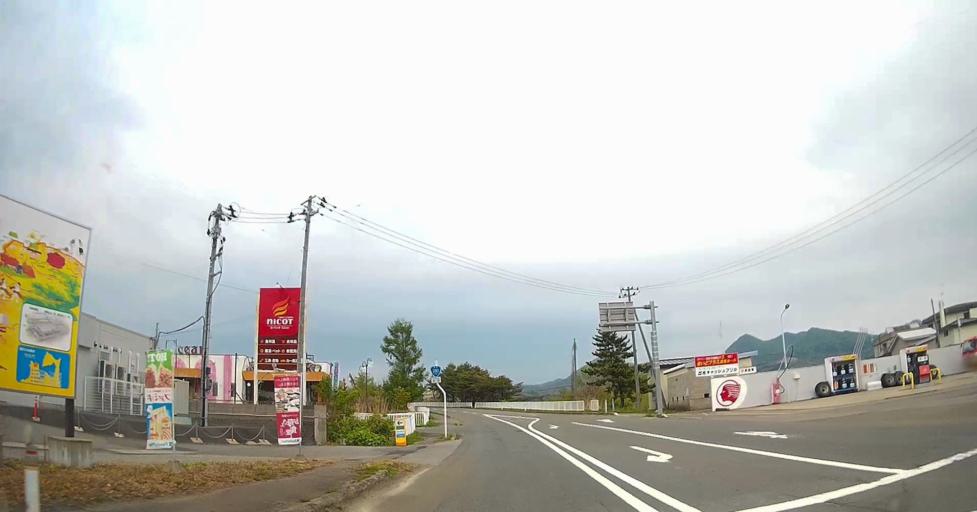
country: JP
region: Aomori
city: Goshogawara
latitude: 41.1765
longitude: 140.4913
